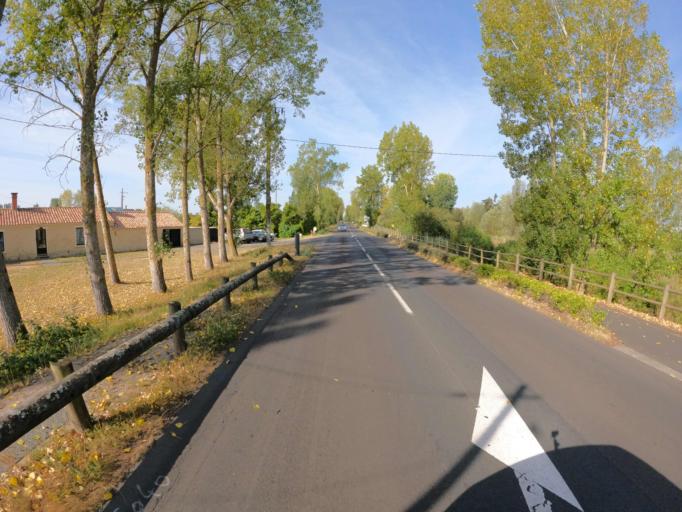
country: FR
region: Pays de la Loire
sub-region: Departement de la Vendee
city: Le Perrier
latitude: 46.8096
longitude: -2.0154
